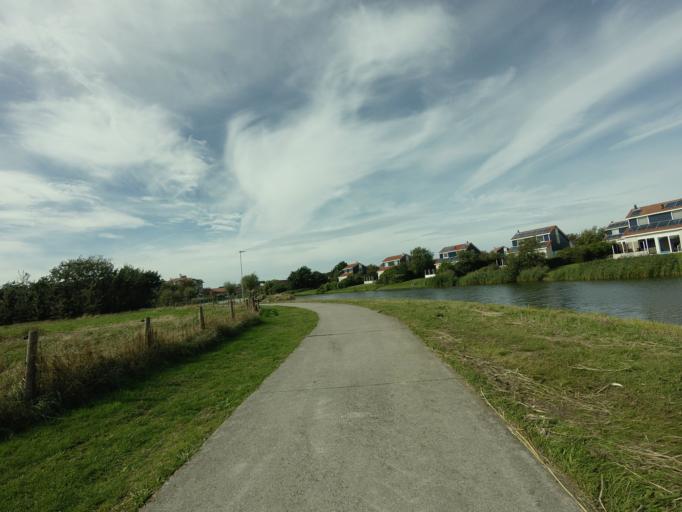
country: NL
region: North Holland
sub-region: Gemeente Texel
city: Den Burg
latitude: 53.0990
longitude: 4.7708
